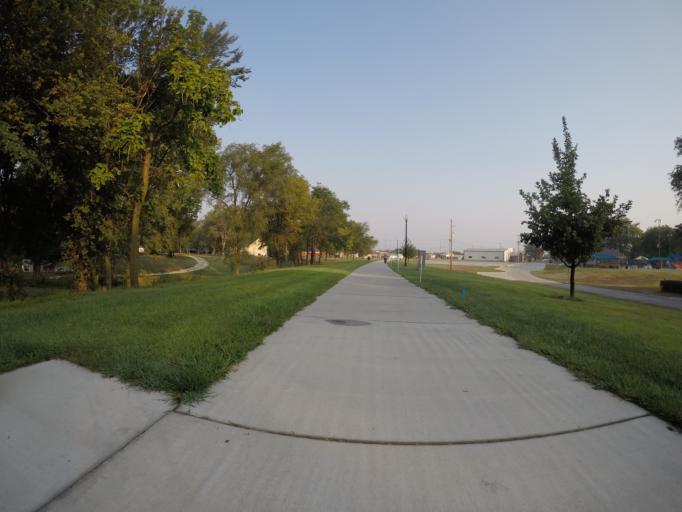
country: US
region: Kansas
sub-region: Marshall County
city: Marysville
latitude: 39.8385
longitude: -96.6479
